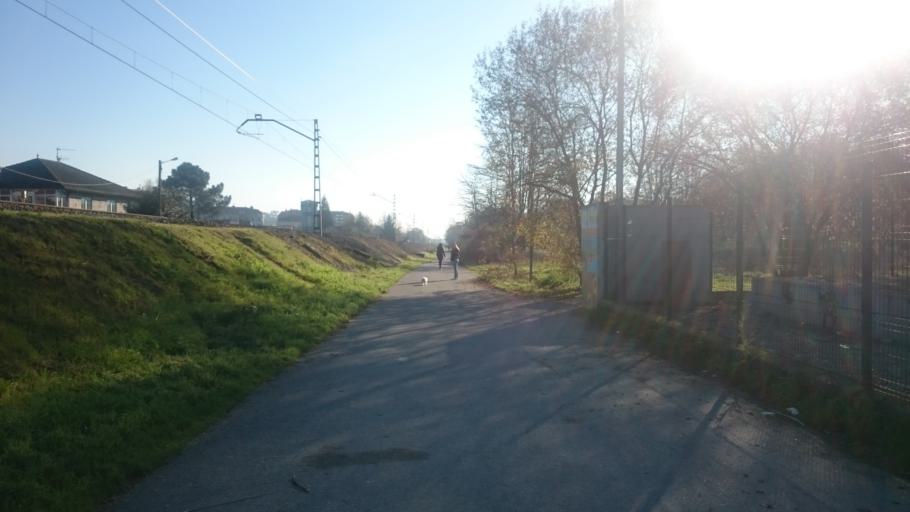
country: ES
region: Galicia
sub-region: Provincia de Pontevedra
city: Porrino
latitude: 42.1578
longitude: -8.6225
